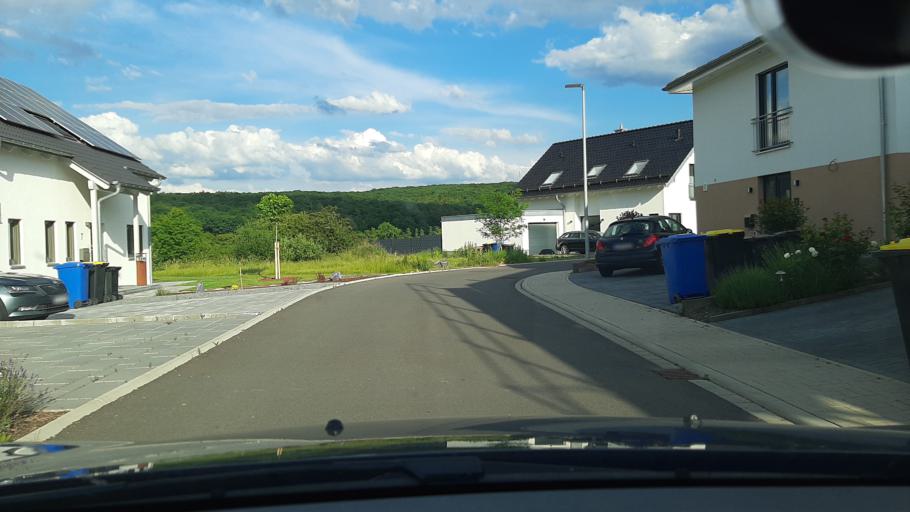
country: DE
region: North Rhine-Westphalia
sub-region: Regierungsbezirk Koln
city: Mechernich
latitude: 50.5906
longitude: 6.6705
